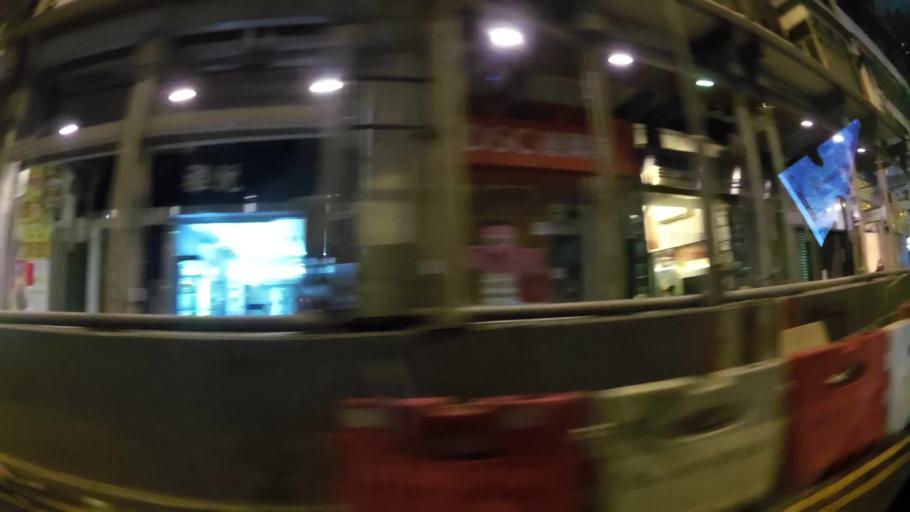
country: HK
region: Kowloon City
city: Kowloon
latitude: 22.3177
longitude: 114.1879
